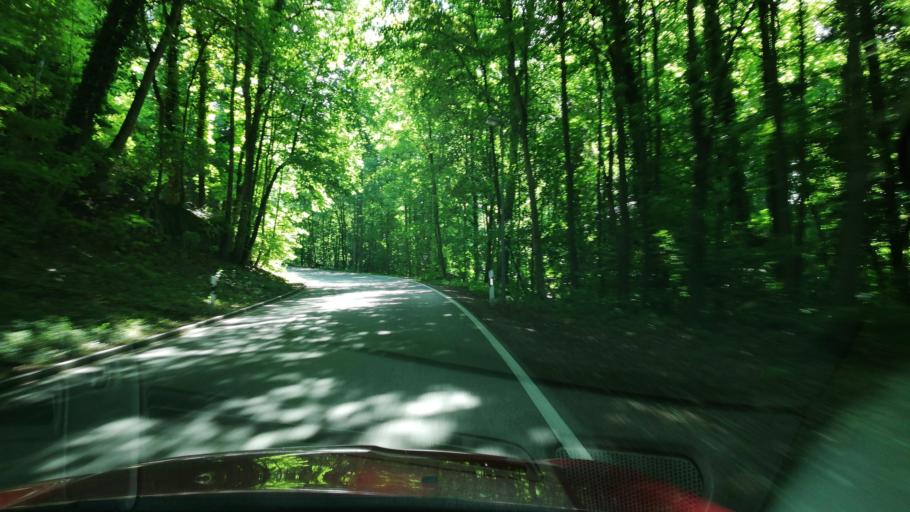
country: DE
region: Bavaria
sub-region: Upper Bavaria
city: Garching an der Alz
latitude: 48.1255
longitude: 12.5939
